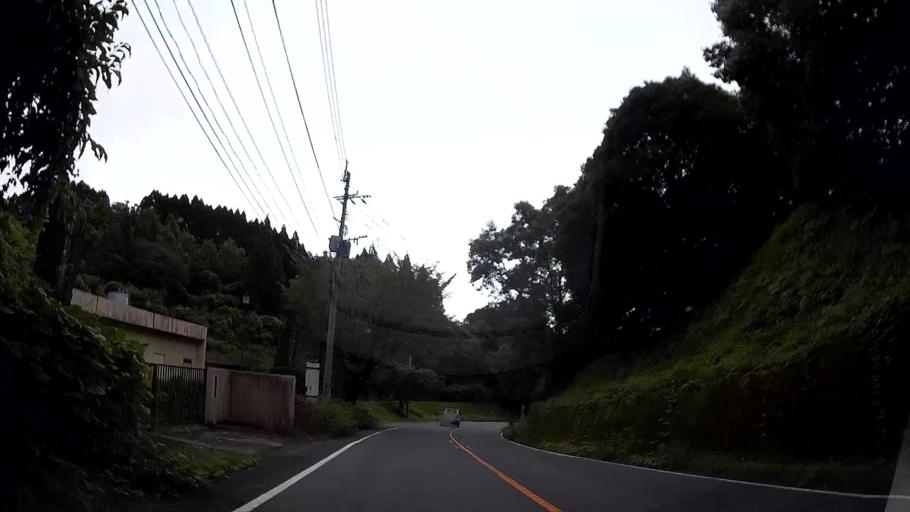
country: JP
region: Kumamoto
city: Kikuchi
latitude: 33.0163
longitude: 130.8685
